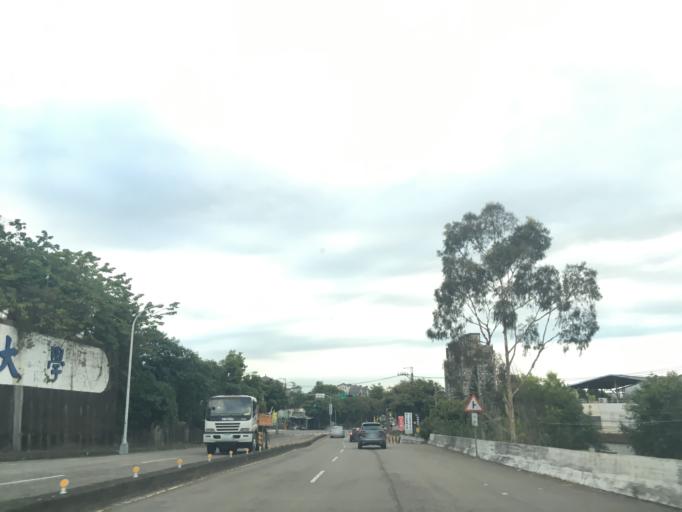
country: TW
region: Taiwan
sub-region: Taichung City
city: Taichung
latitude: 24.1731
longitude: 120.7343
